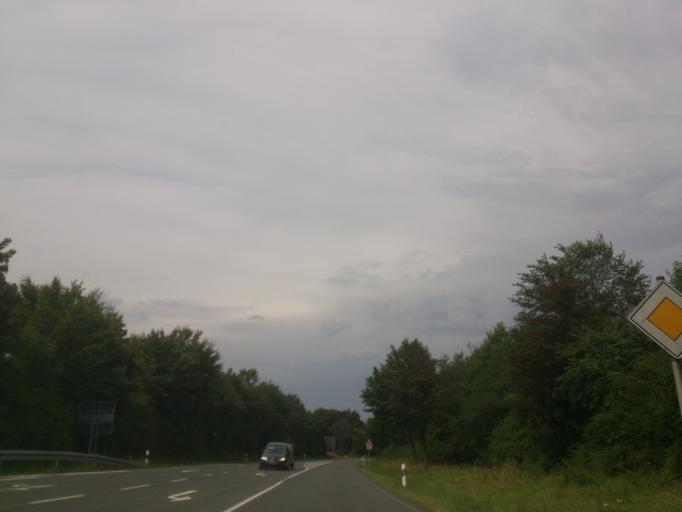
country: DE
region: North Rhine-Westphalia
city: Lichtenau
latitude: 51.5630
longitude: 8.8370
